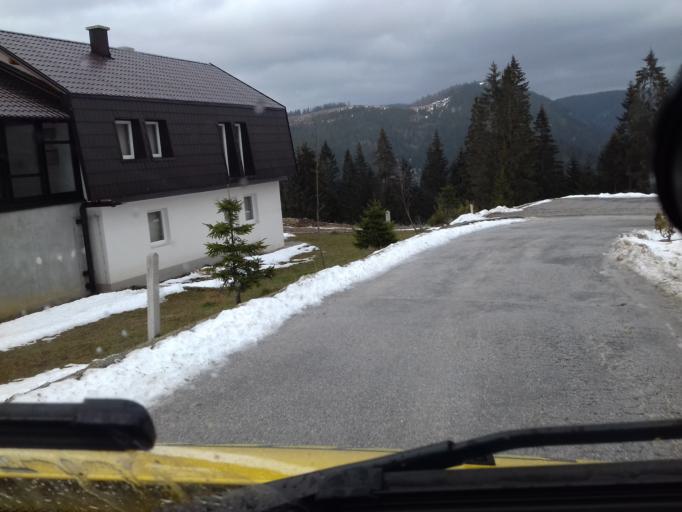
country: BA
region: Federation of Bosnia and Herzegovina
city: Turbe
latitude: 44.3153
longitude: 17.5822
